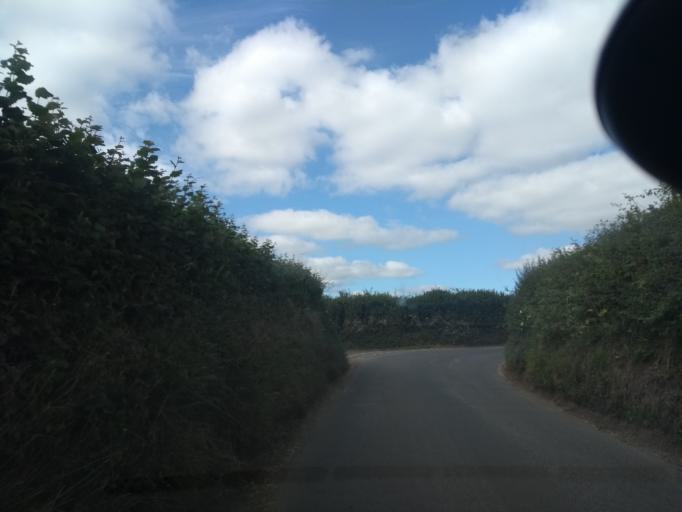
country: GB
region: England
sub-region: Devon
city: Modbury
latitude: 50.3090
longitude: -3.8816
